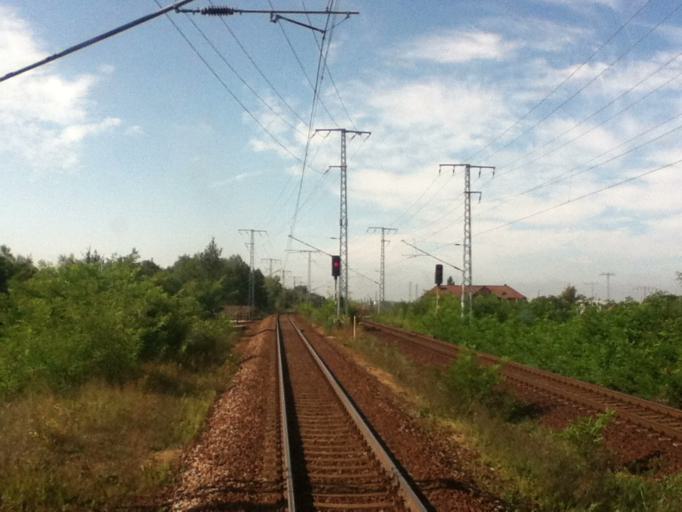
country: DE
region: Brandenburg
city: Senftenberg
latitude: 51.5400
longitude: 14.0309
